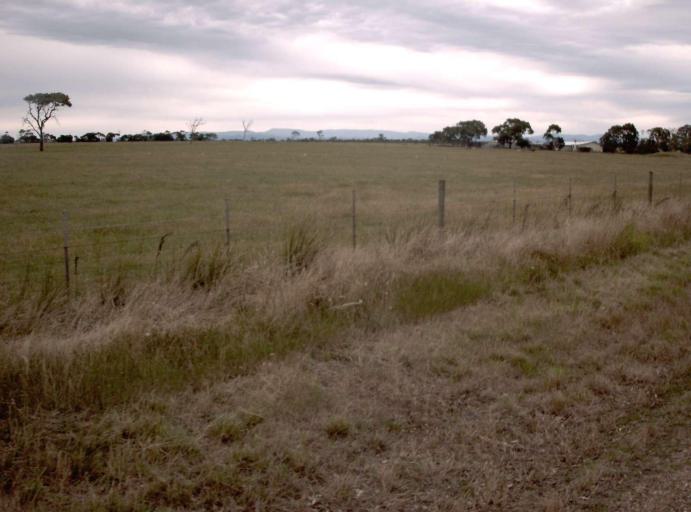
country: AU
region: Victoria
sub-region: Wellington
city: Sale
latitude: -37.9985
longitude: 147.1917
